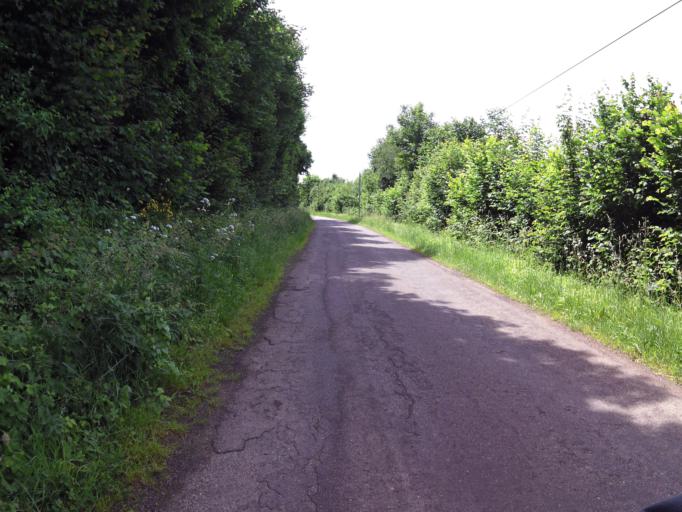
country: FR
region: Champagne-Ardenne
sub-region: Departement des Ardennes
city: Mouzon
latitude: 49.5305
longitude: 5.1076
